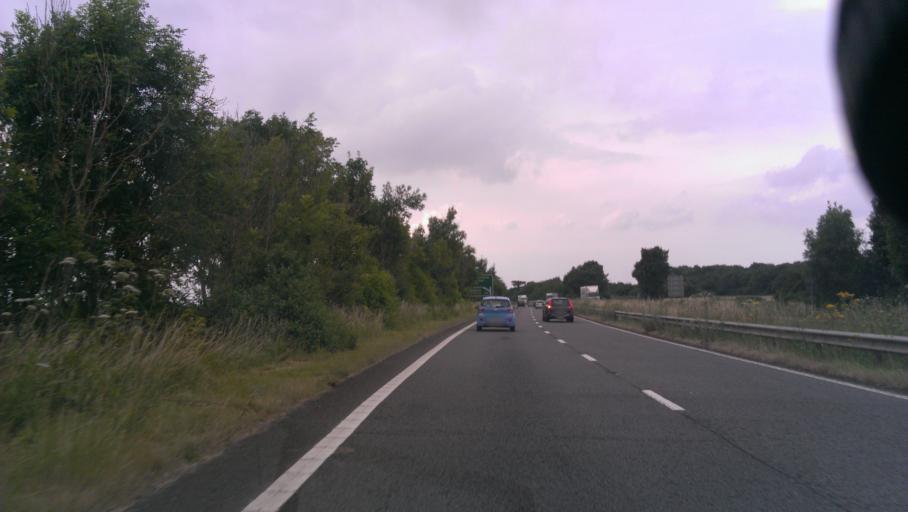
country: GB
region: England
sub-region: Kent
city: Wootton
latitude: 51.1882
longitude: 1.1897
